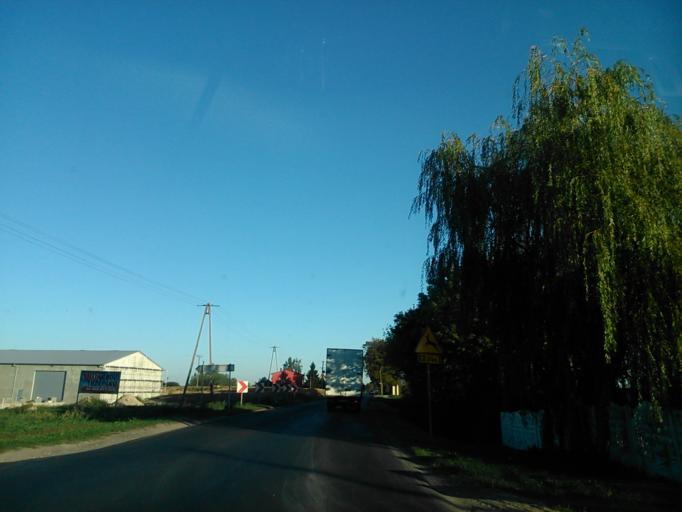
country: PL
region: Kujawsko-Pomorskie
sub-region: Powiat golubsko-dobrzynski
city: Golub-Dobrzyn
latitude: 53.1359
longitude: 19.0070
